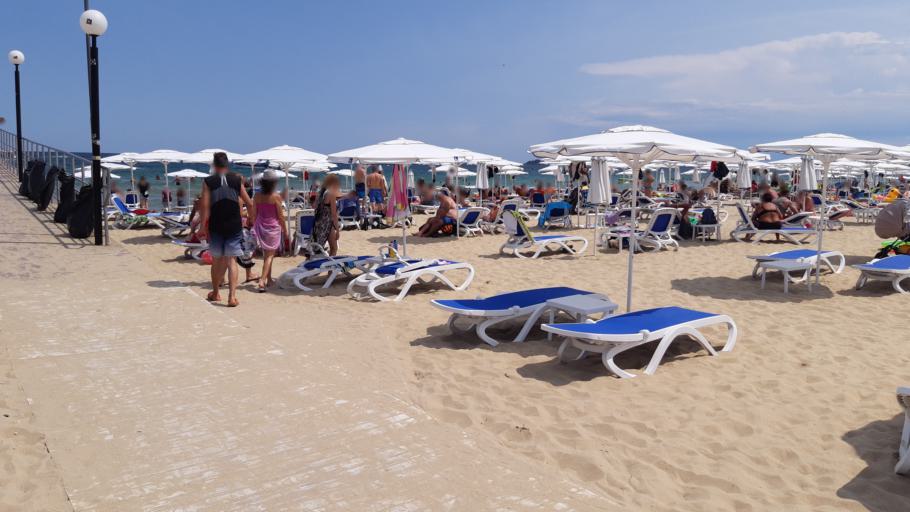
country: BG
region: Burgas
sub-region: Obshtina Nesebur
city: Nesebar
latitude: 42.6940
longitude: 27.7153
